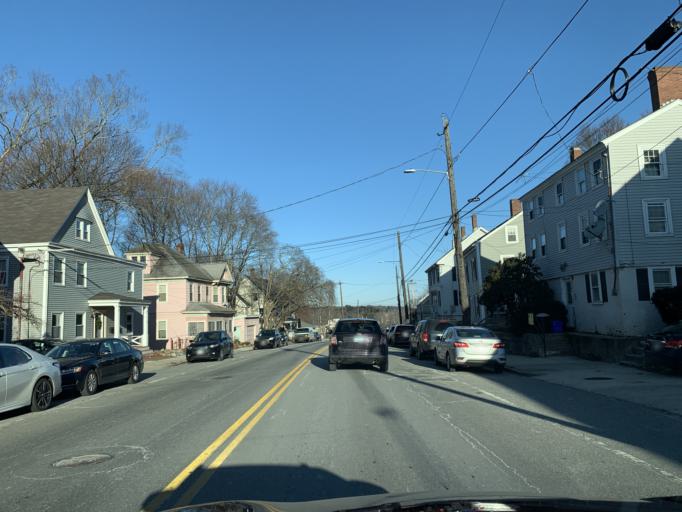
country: US
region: Massachusetts
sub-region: Essex County
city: Andover
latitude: 42.6592
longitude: -71.1427
